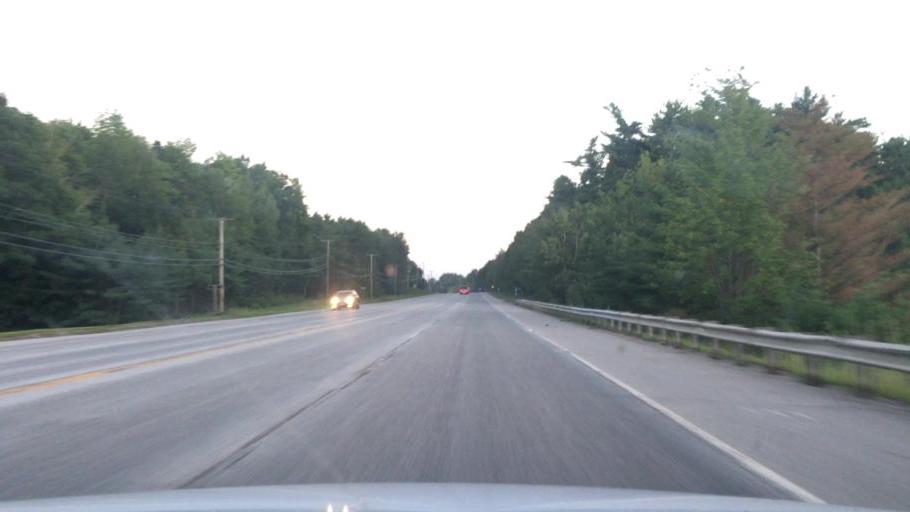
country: US
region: Maine
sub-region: Androscoggin County
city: Auburn
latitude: 44.1526
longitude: -70.2321
